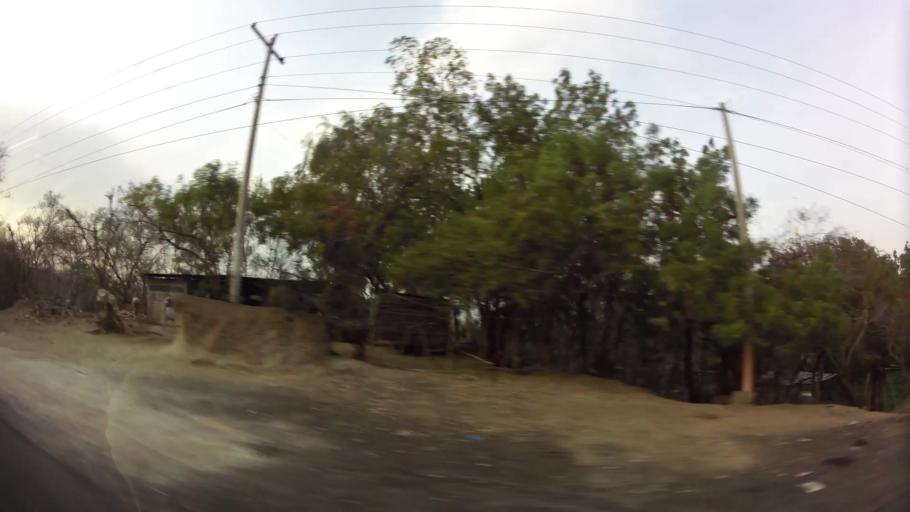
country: NI
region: Managua
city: Ciudad Sandino
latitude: 12.2409
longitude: -86.4386
